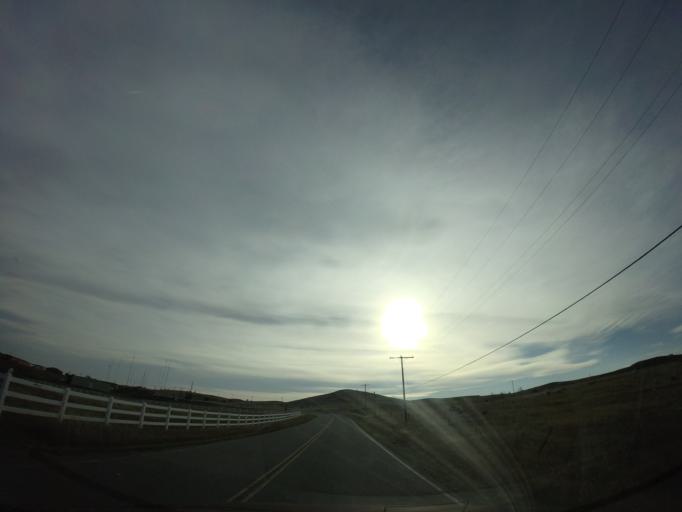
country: US
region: Montana
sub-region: Yellowstone County
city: Billings
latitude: 45.7777
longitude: -108.4624
